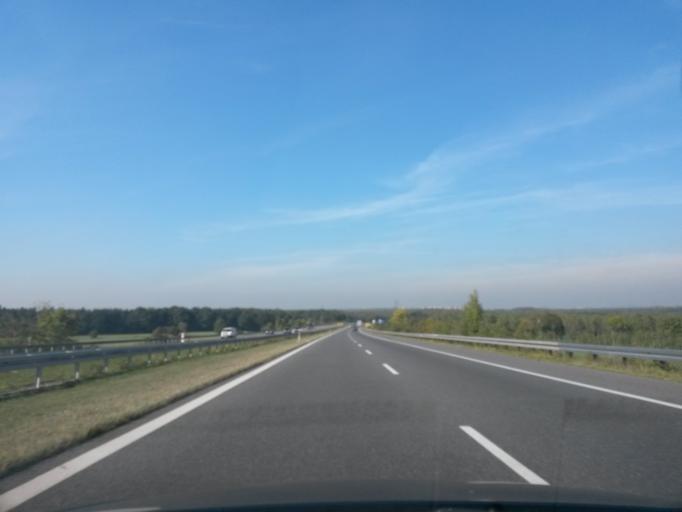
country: PL
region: Silesian Voivodeship
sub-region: Powiat bierunsko-ledzinski
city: Imielin
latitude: 50.1780
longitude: 19.2014
